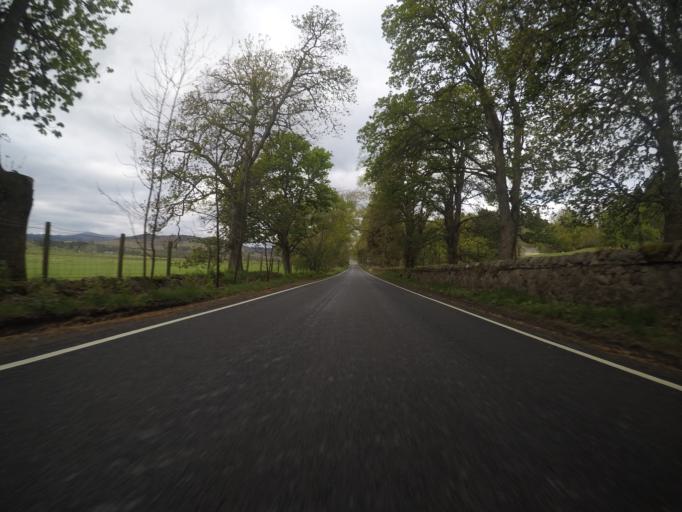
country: GB
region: Scotland
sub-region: Highland
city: Kingussie
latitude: 57.0181
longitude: -4.2334
